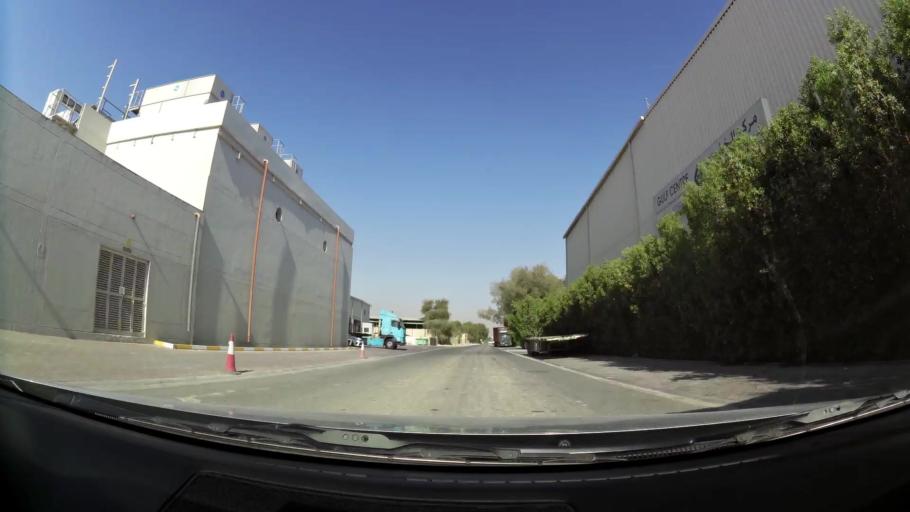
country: AE
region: Dubai
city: Dubai
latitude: 24.9939
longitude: 55.1009
